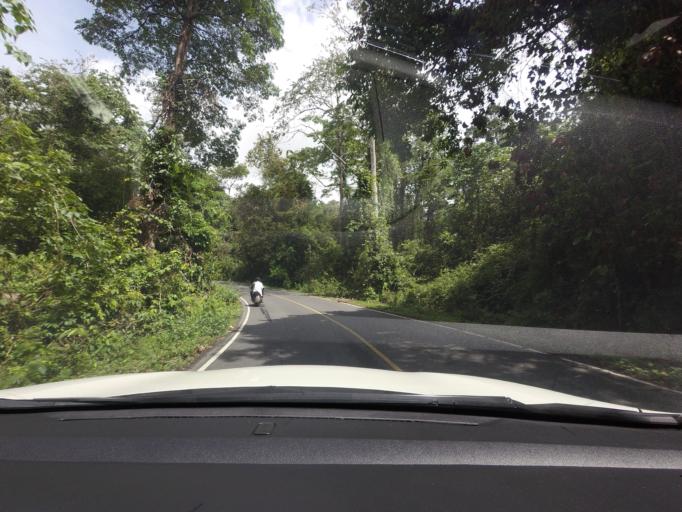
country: TH
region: Nakhon Nayok
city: Pak Phli
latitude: 14.3212
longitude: 101.3712
